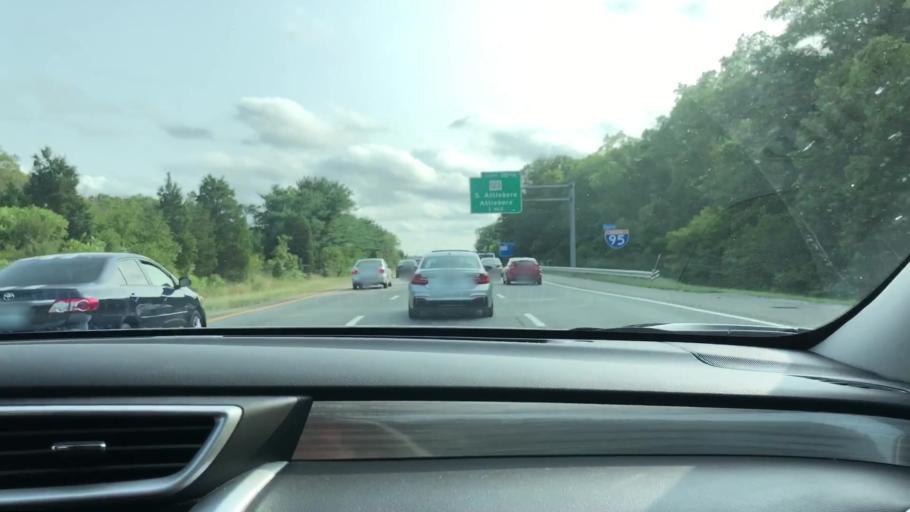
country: US
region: Massachusetts
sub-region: Bristol County
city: Attleboro
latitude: 41.9505
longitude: -71.3077
